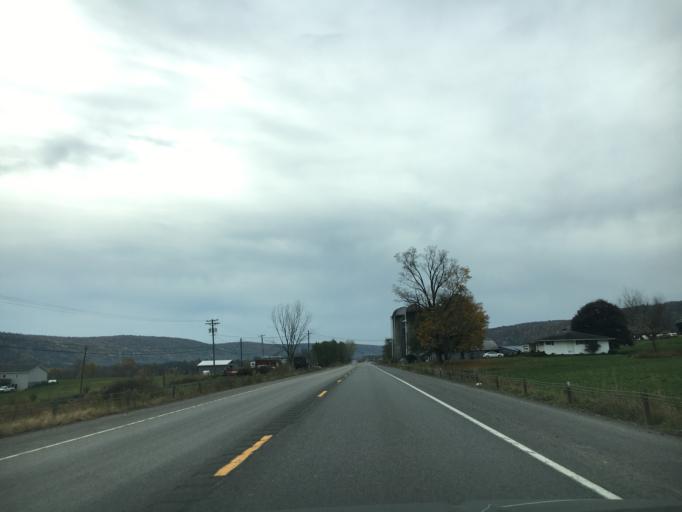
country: US
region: New York
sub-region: Otsego County
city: Cooperstown
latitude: 42.5782
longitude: -74.9489
